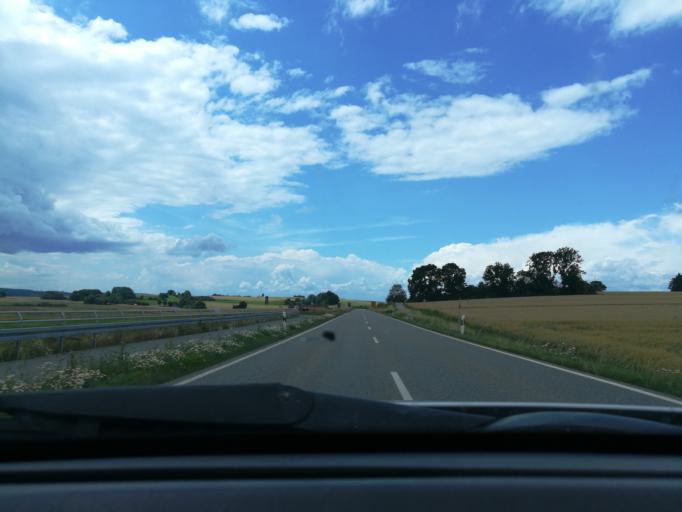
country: DE
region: Baden-Wuerttemberg
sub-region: Freiburg Region
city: Bosingen
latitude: 48.2030
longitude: 8.5451
